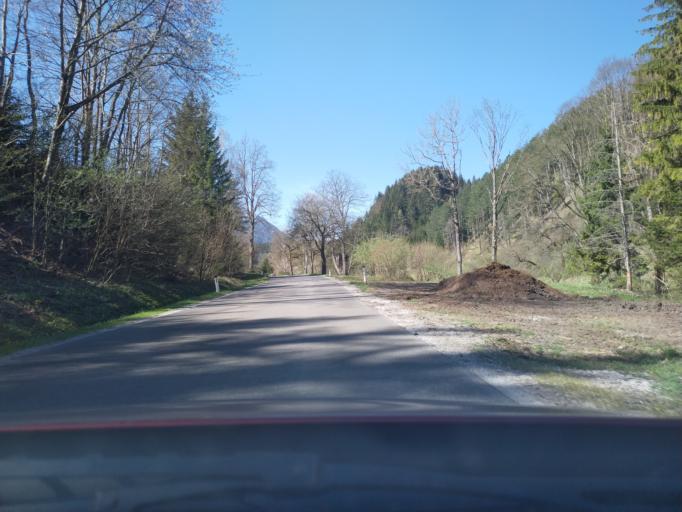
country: AT
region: Lower Austria
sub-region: Politischer Bezirk Wiener Neustadt
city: Gutenstein
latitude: 47.8178
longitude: 15.8141
